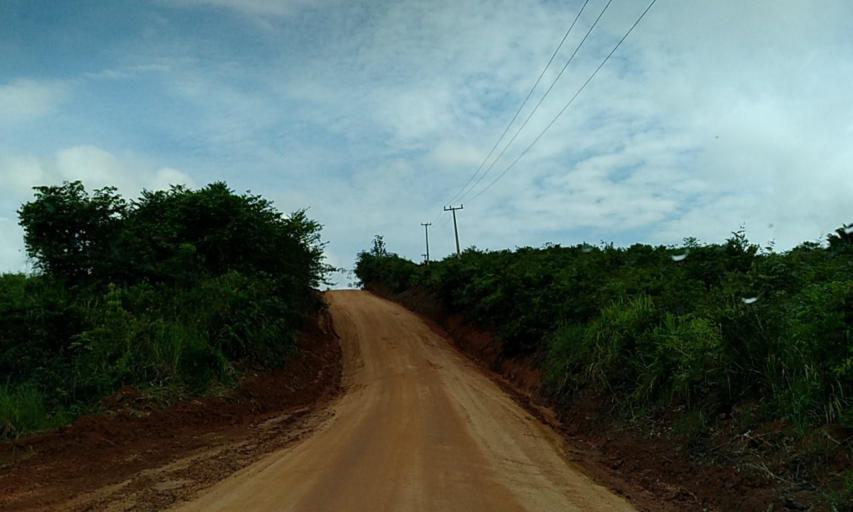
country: BR
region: Para
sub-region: Altamira
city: Altamira
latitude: -3.0830
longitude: -51.6347
